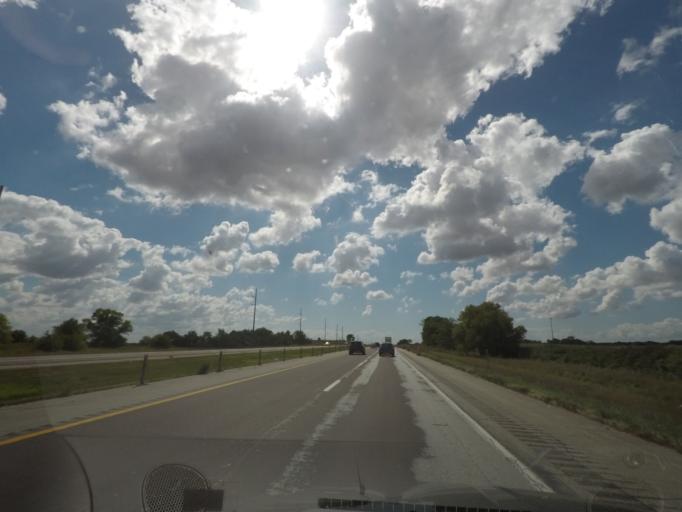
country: US
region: Iowa
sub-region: Story County
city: Huxley
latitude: 41.9238
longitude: -93.5705
